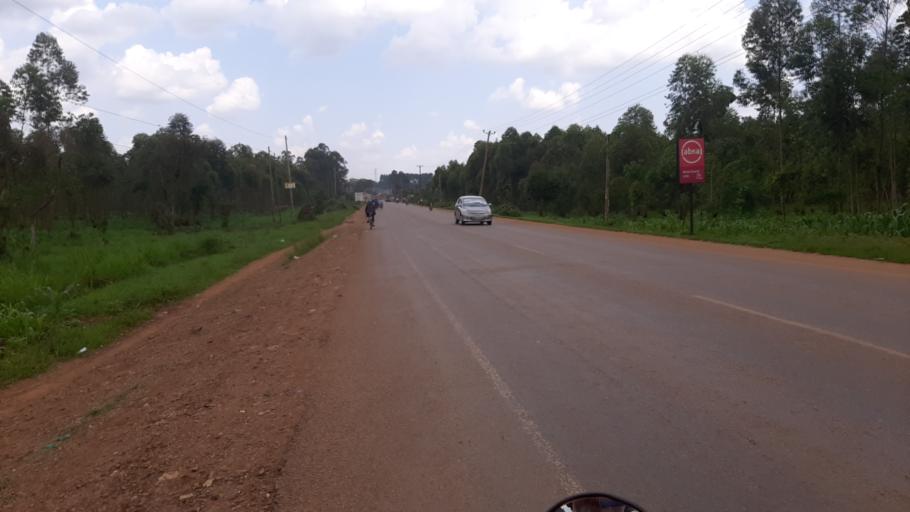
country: UG
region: Eastern Region
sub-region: Mbale District
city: Mbale
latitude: 1.0545
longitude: 34.1794
